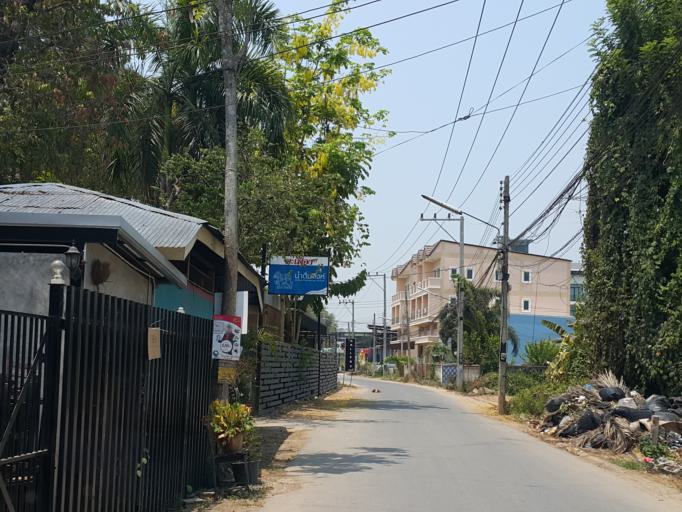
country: TH
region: Phitsanulok
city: Phitsanulok
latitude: 16.8115
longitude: 100.2566
